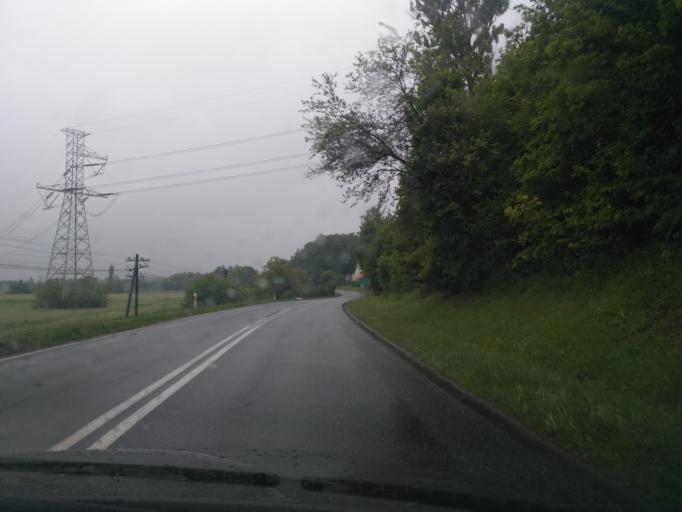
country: PL
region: Subcarpathian Voivodeship
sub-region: Powiat krosnienski
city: Leki
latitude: 49.8067
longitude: 21.6393
